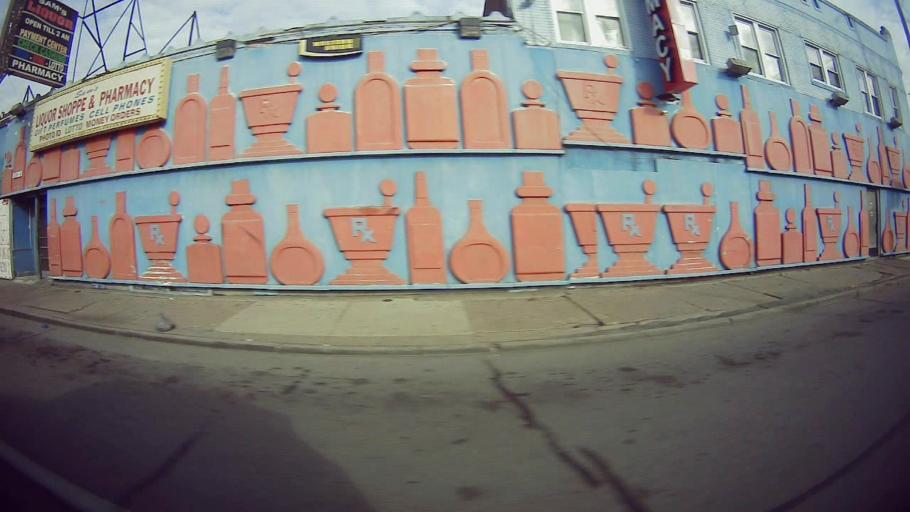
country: US
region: Michigan
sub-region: Oakland County
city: Oak Park
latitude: 42.4019
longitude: -83.1848
